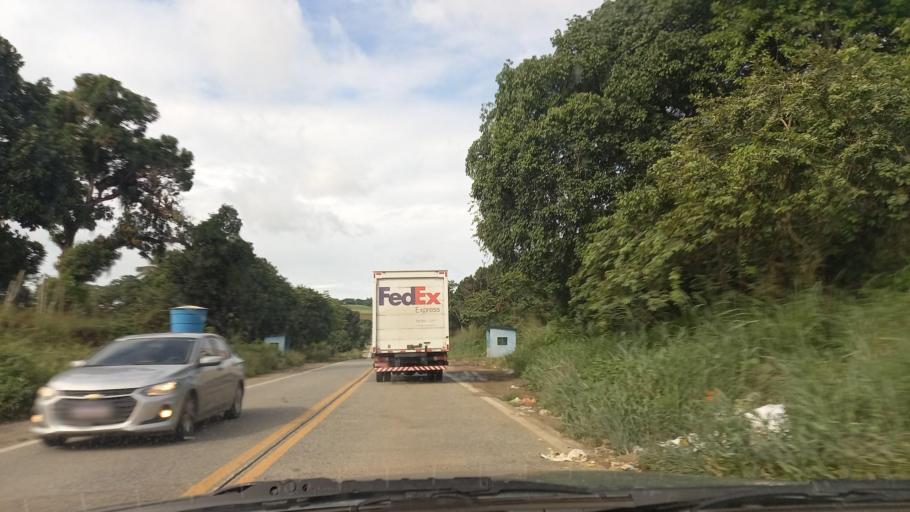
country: BR
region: Pernambuco
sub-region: Catende
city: Catende
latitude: -8.6920
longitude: -35.6780
